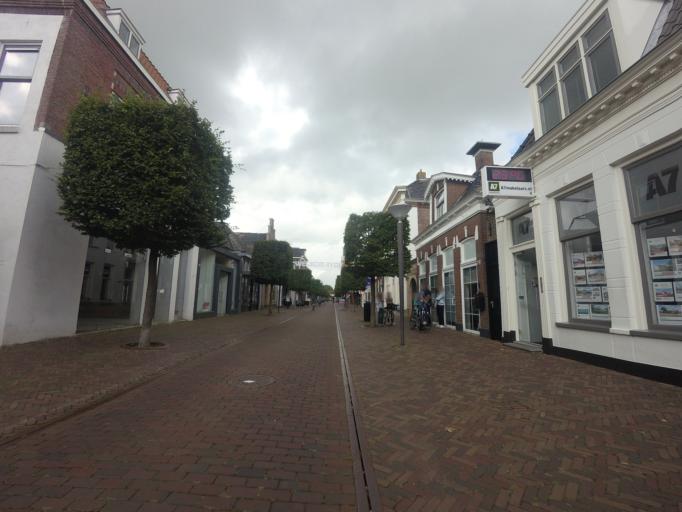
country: NL
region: Friesland
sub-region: Gemeente Skarsterlan
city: Joure
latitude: 52.9671
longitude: 5.7964
